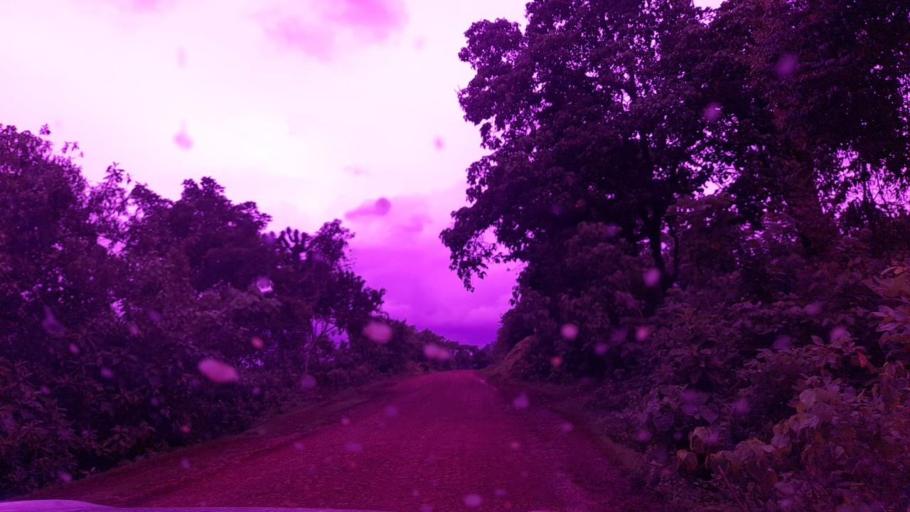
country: ET
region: Southern Nations, Nationalities, and People's Region
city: Tippi
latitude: 7.5810
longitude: 35.6672
